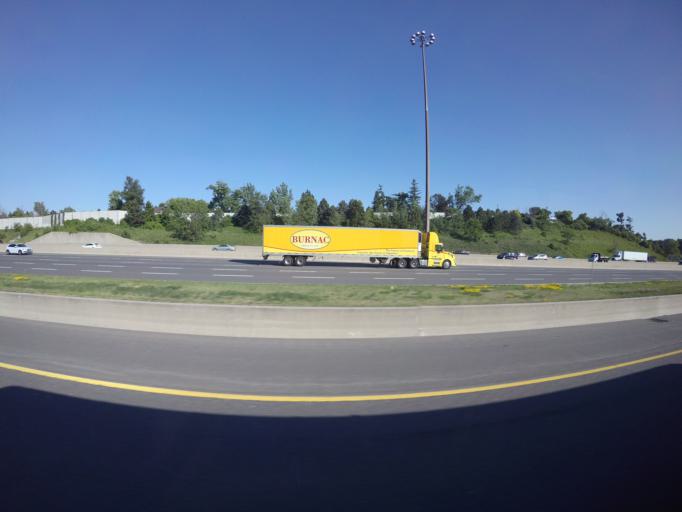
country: CA
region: Ontario
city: Pickering
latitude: 43.8068
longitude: -79.1317
